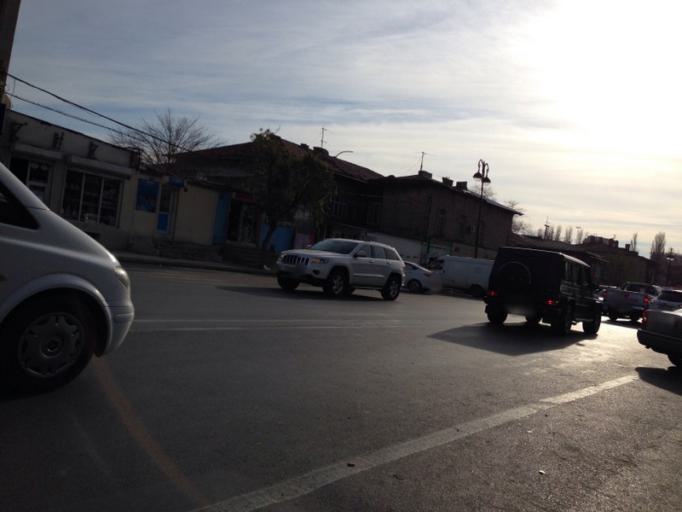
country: AZ
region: Baki
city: Baku
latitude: 40.3856
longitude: 49.8548
